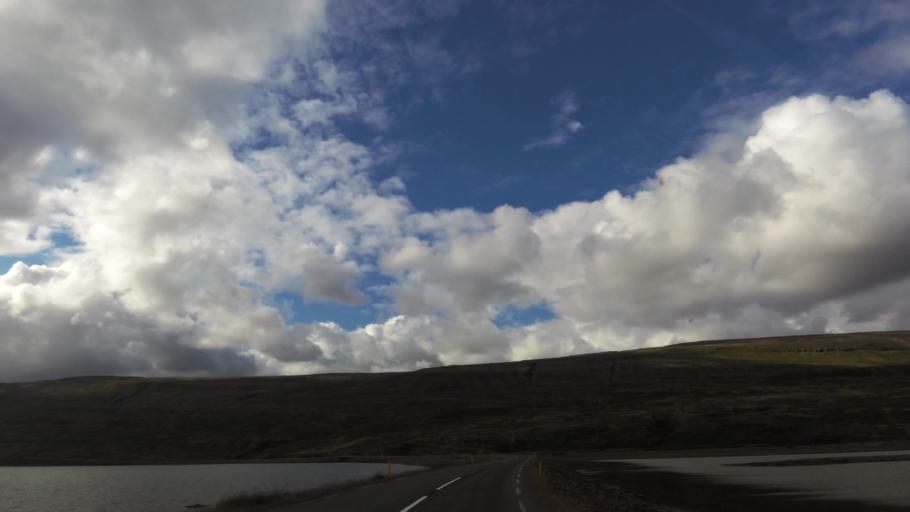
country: IS
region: West
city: Olafsvik
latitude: 65.5328
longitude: -23.7858
